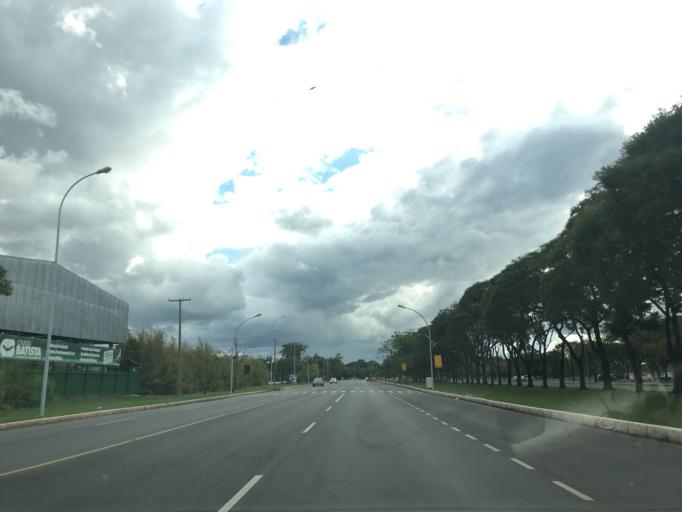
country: BR
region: Federal District
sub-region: Brasilia
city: Brasilia
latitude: -15.8023
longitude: -47.9040
